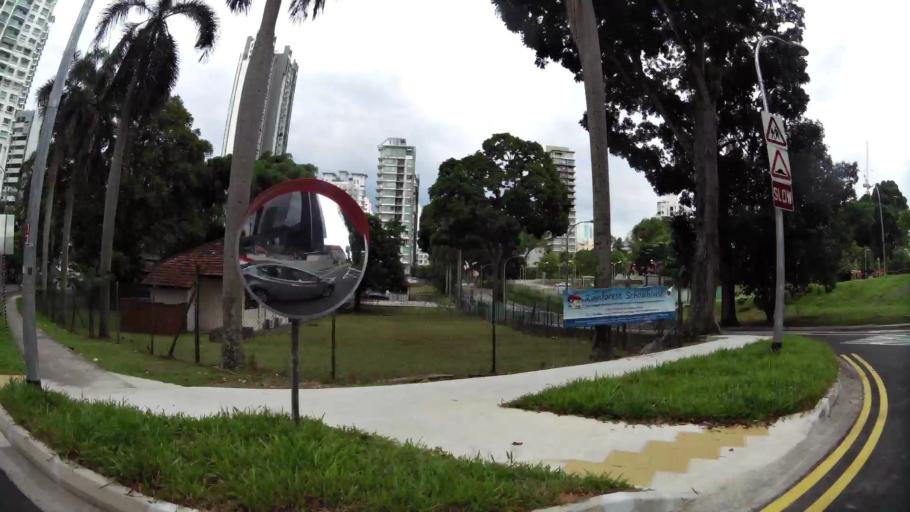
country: SG
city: Singapore
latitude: 1.3222
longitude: 103.8493
